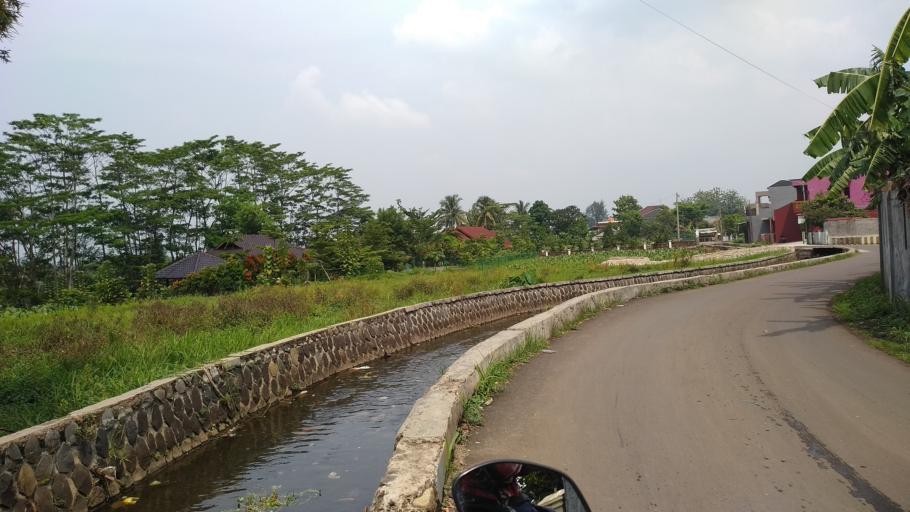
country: ID
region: West Java
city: Ciampea
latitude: -6.5569
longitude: 106.7459
